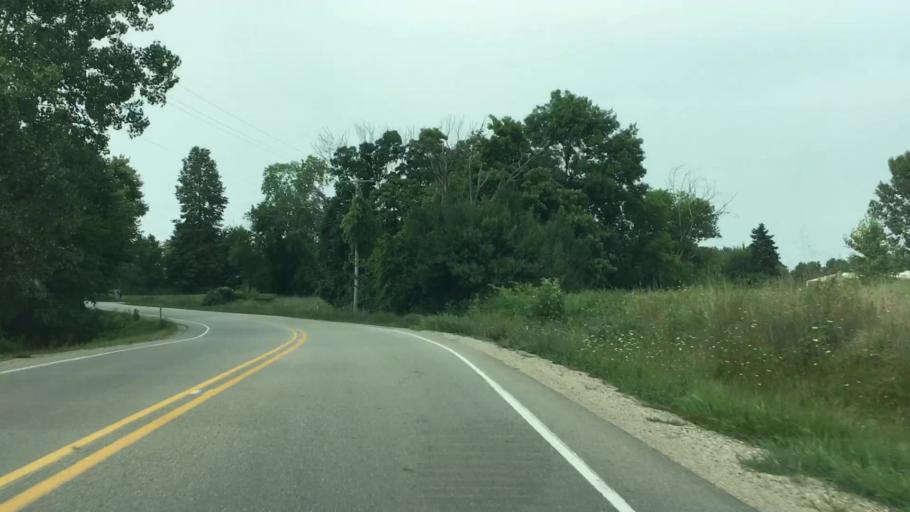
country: US
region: Michigan
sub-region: Ottawa County
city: Hudsonville
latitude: 42.8377
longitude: -85.9004
